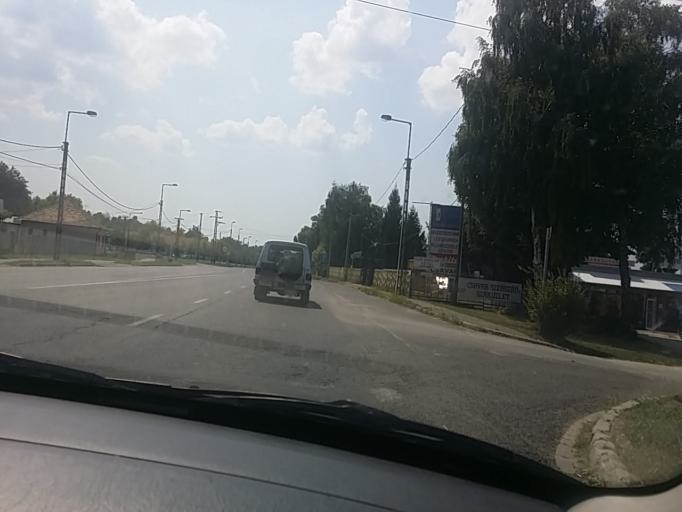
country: HU
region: Tolna
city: Dombovar
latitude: 46.3898
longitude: 18.1438
